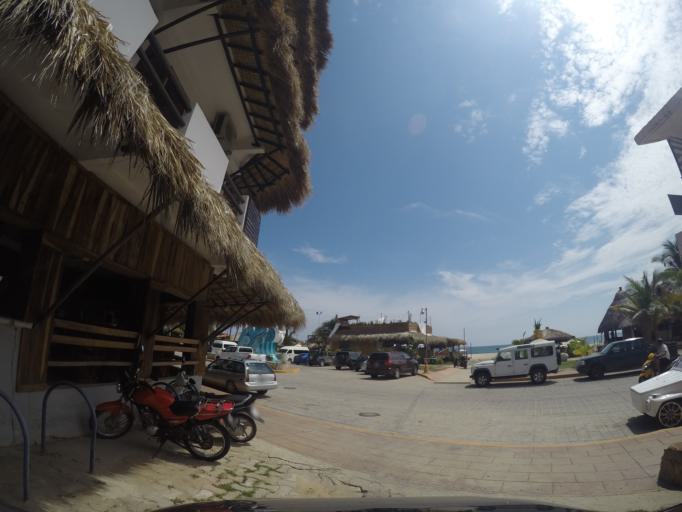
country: MX
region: Oaxaca
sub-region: Santa Maria Colotepec
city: Brisas de Zicatela
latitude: 15.8544
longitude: -97.0561
